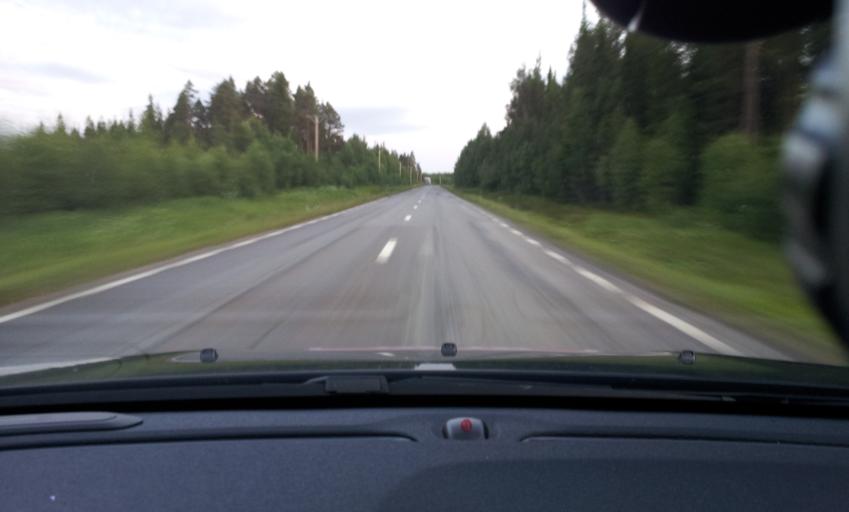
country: SE
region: Jaemtland
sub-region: Ragunda Kommun
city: Hammarstrand
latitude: 63.0071
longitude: 16.1168
